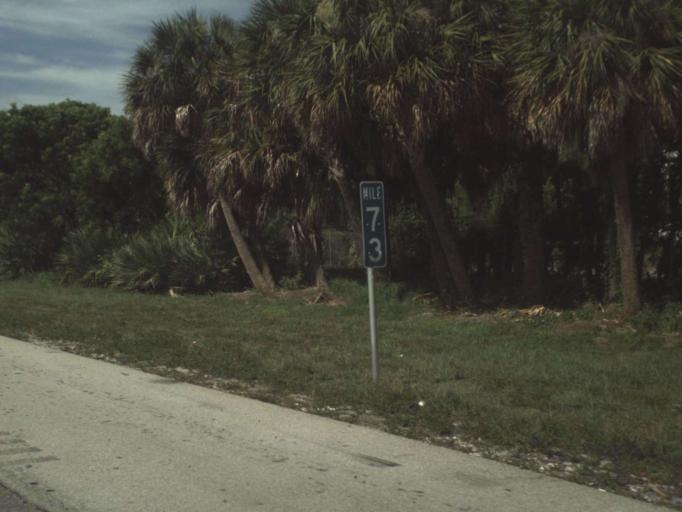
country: US
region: Florida
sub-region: Palm Beach County
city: Mangonia Park
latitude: 26.7427
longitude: -80.0908
